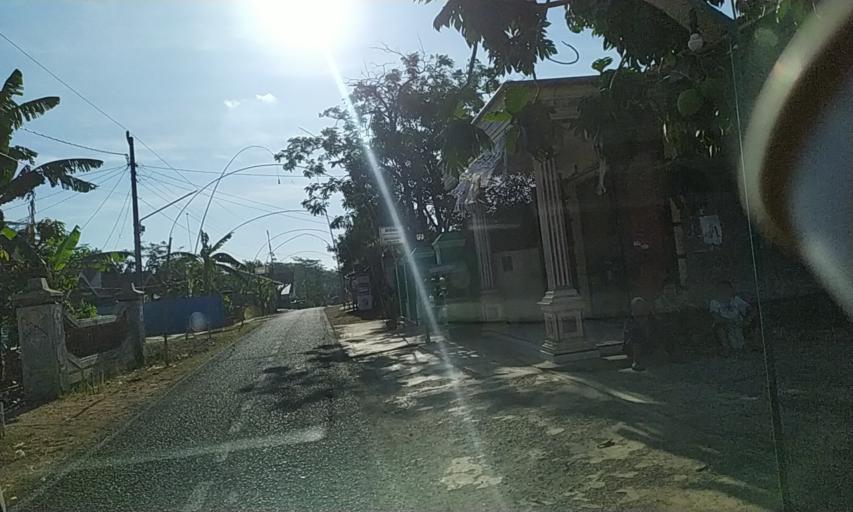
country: ID
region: Central Java
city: Bayeman
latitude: -7.6200
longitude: 109.2245
